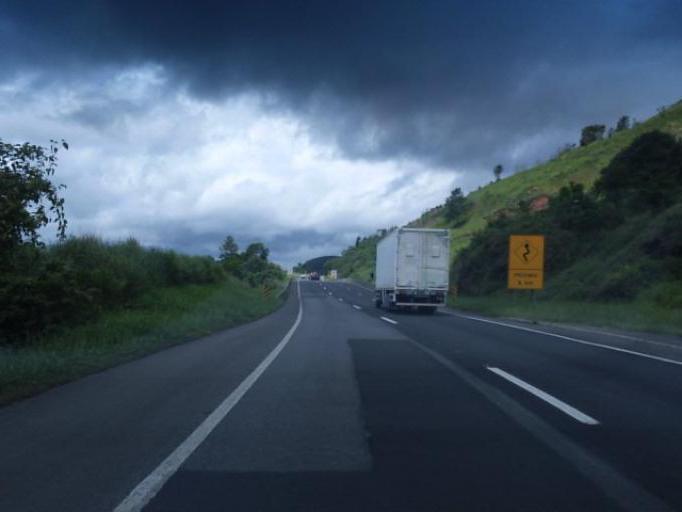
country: BR
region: Sao Paulo
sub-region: Cajati
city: Cajati
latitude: -24.9688
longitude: -48.4841
